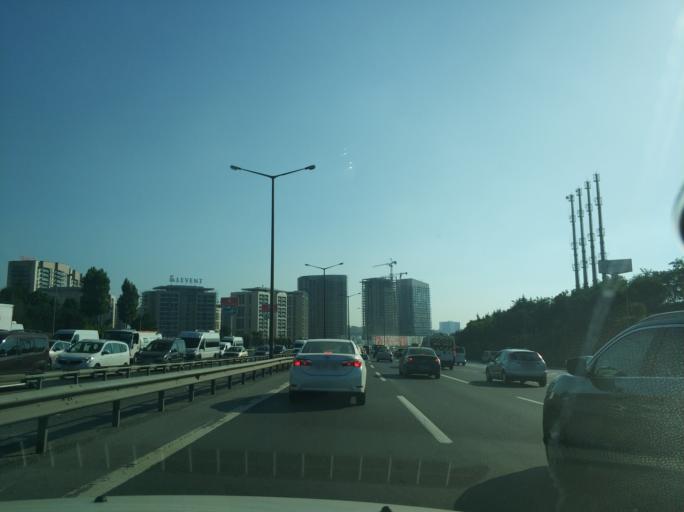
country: TR
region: Istanbul
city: Sisli
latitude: 41.0952
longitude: 28.9508
